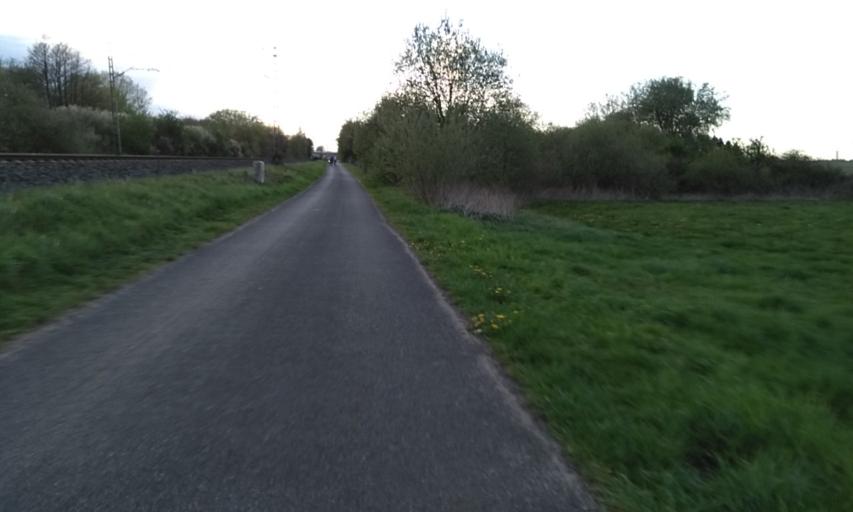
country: DE
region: Lower Saxony
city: Nottensdorf
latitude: 53.4947
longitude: 9.6063
